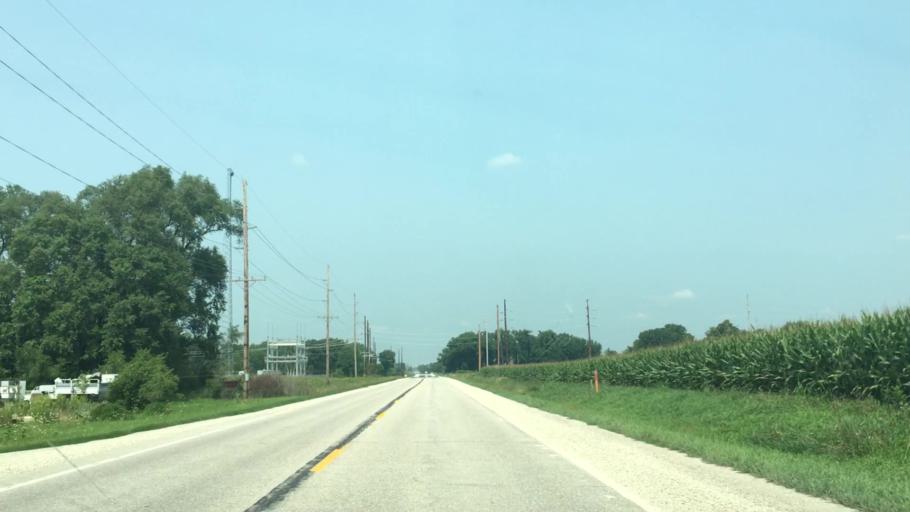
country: US
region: Iowa
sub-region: Buchanan County
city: Independence
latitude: 42.3761
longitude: -91.8894
